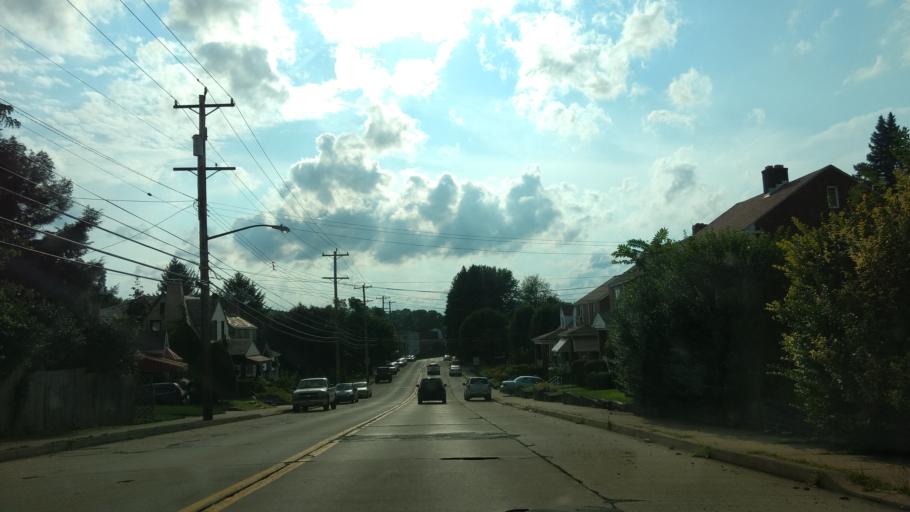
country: US
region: Pennsylvania
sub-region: Allegheny County
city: Bellevue
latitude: 40.4844
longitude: -80.0373
